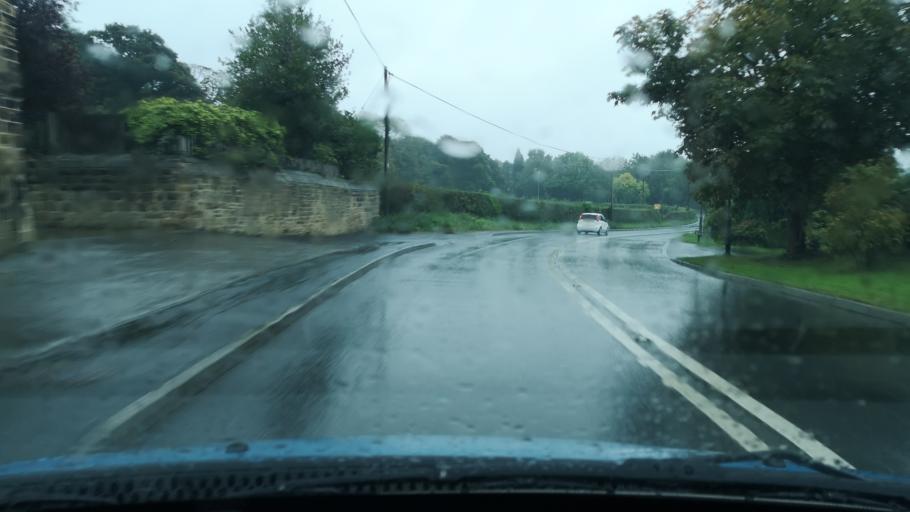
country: GB
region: England
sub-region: City and Borough of Wakefield
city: Fitzwilliam
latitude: 53.6486
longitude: -1.3785
